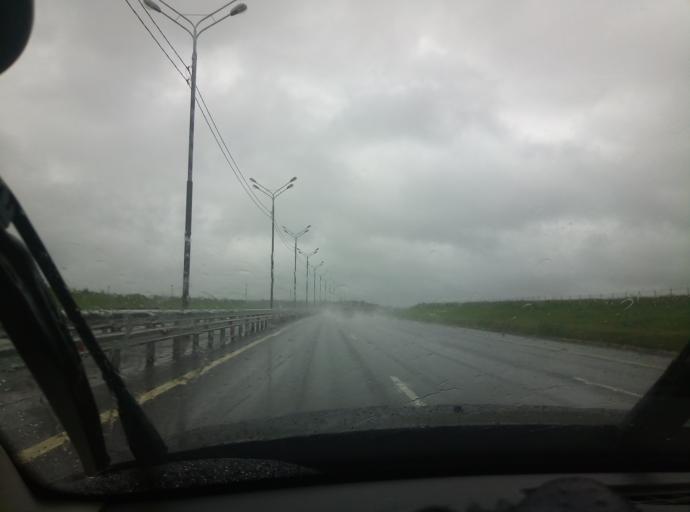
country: RU
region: Moskovskaya
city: Danki
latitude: 54.9432
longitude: 37.5304
